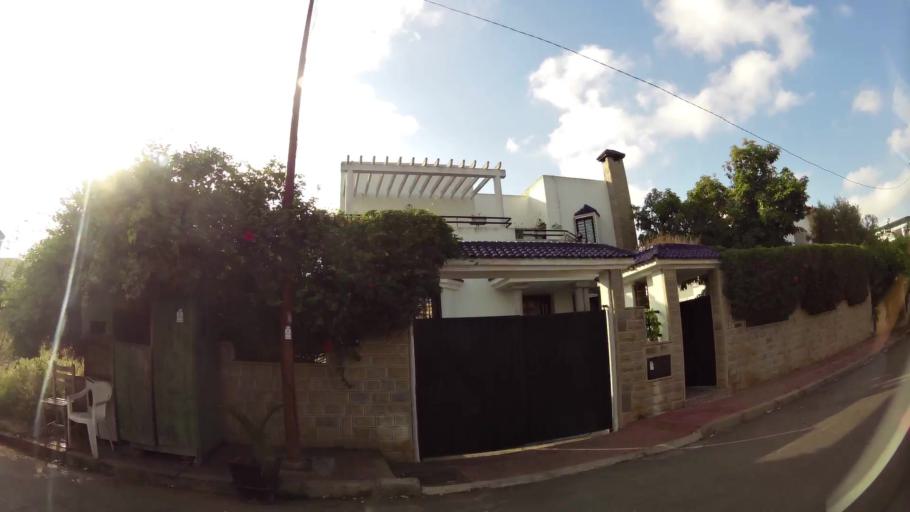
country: MA
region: Rabat-Sale-Zemmour-Zaer
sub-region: Skhirate-Temara
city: Temara
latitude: 33.9561
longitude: -6.8602
